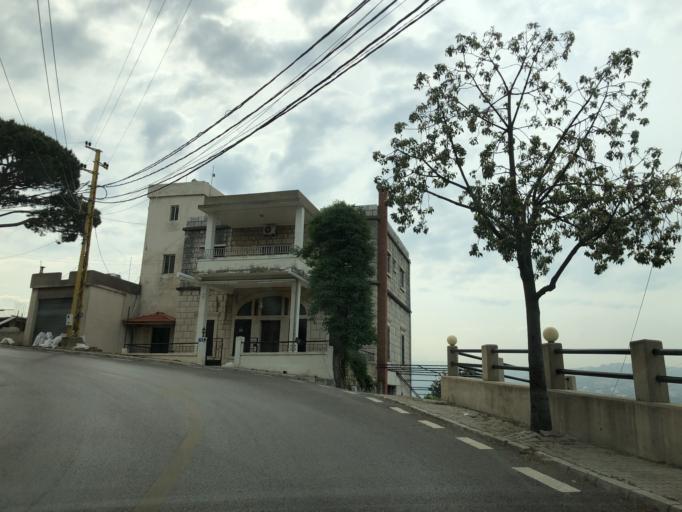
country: LB
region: Mont-Liban
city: Jdaidet el Matn
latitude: 33.8585
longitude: 35.6013
